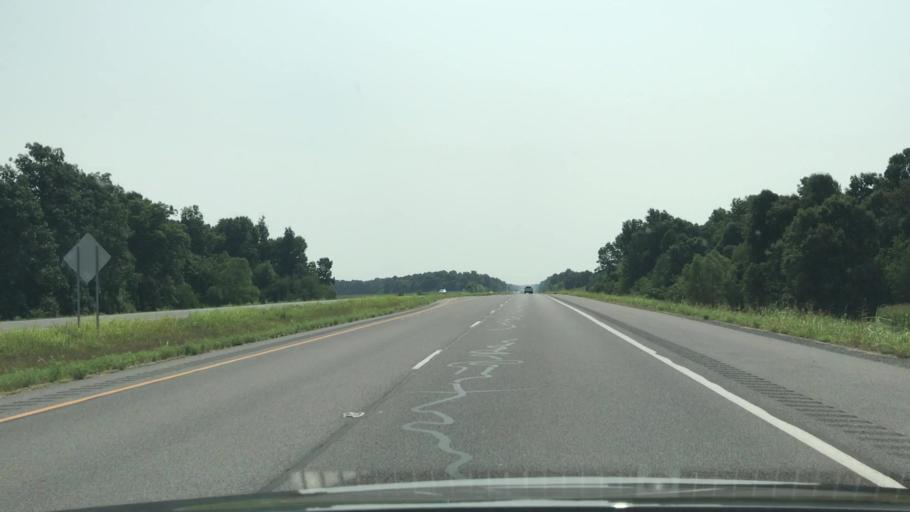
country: US
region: Kentucky
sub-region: Graves County
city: Mayfield
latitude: 36.6767
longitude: -88.5210
